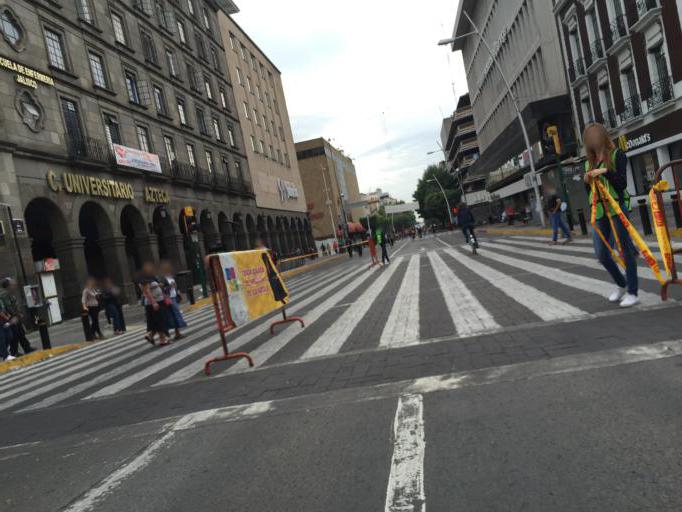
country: MX
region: Jalisco
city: Guadalajara
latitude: 20.6751
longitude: -103.3483
